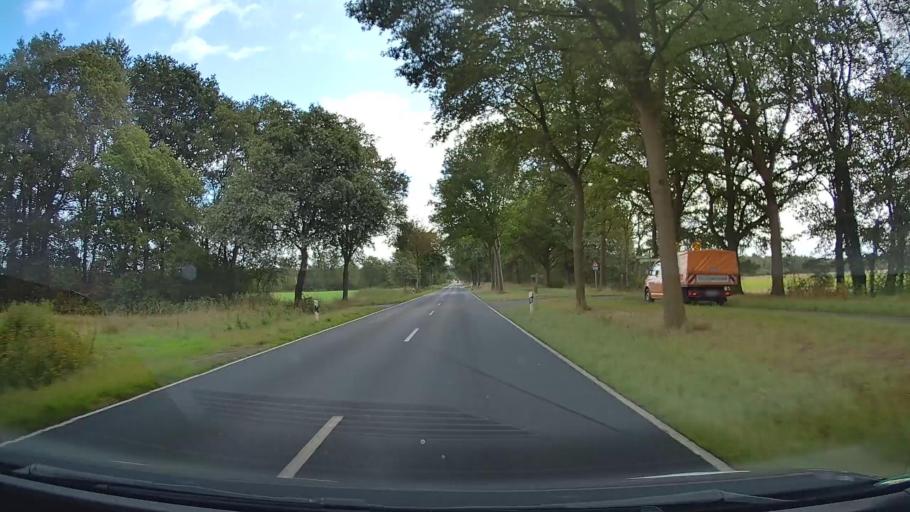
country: DE
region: Lower Saxony
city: Rhade
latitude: 53.3451
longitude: 9.0821
